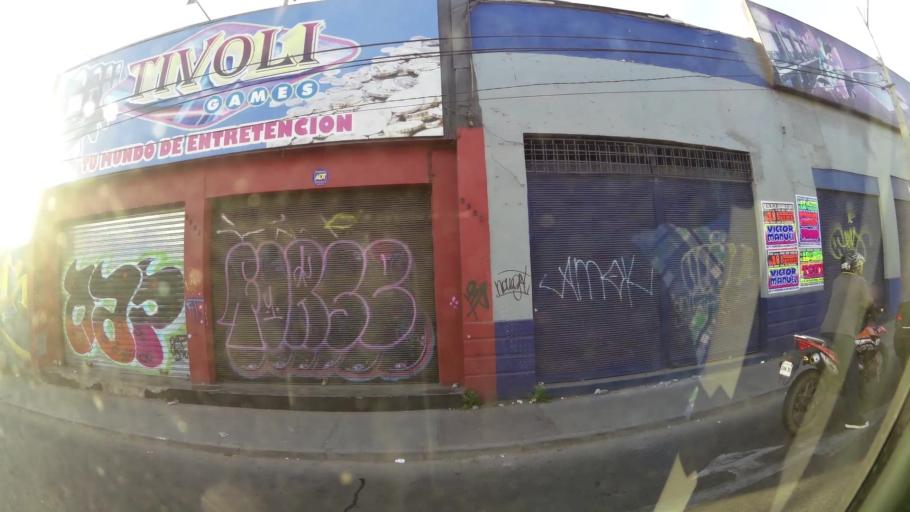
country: CL
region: Santiago Metropolitan
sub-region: Provincia de Santiago
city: Santiago
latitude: -33.4358
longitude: -70.6805
